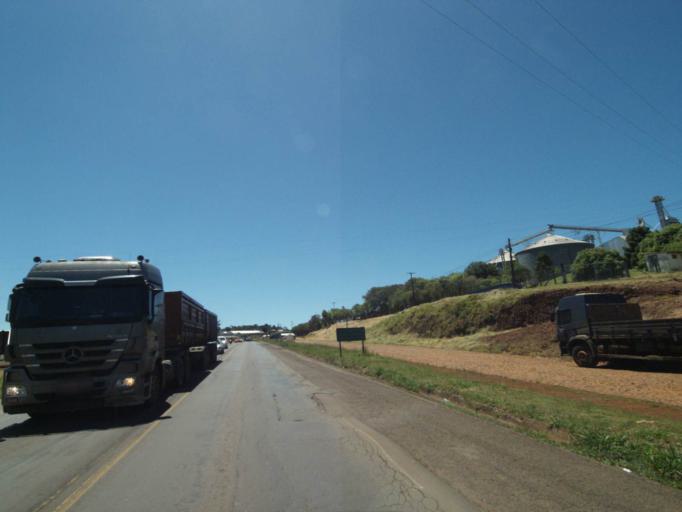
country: BR
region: Parana
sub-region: Pato Branco
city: Pato Branco
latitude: -26.2590
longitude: -52.7723
